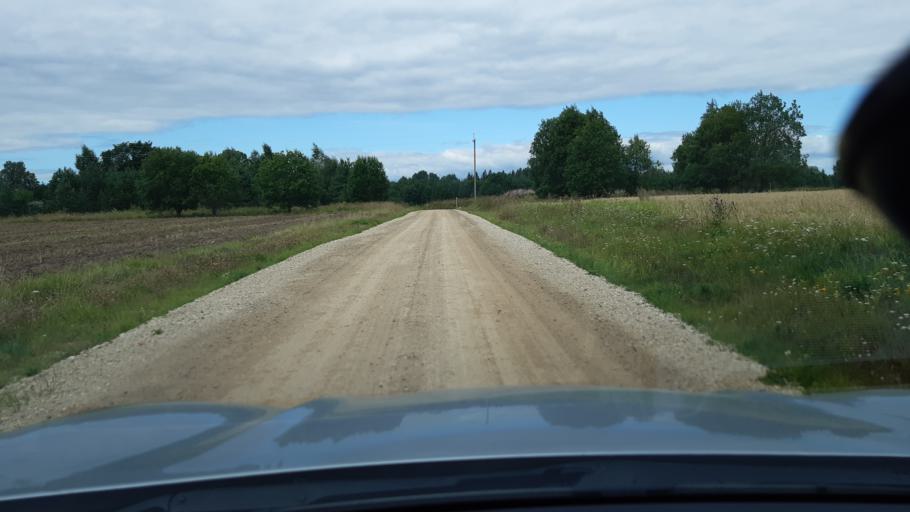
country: EE
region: Raplamaa
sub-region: Jaervakandi vald
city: Jarvakandi
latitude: 58.8051
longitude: 24.8468
